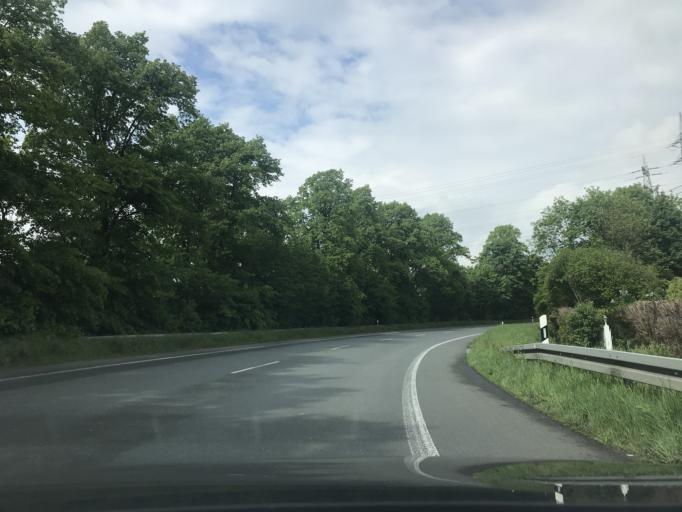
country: DE
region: North Rhine-Westphalia
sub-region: Regierungsbezirk Arnsberg
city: Hagen
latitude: 51.4102
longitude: 7.4949
